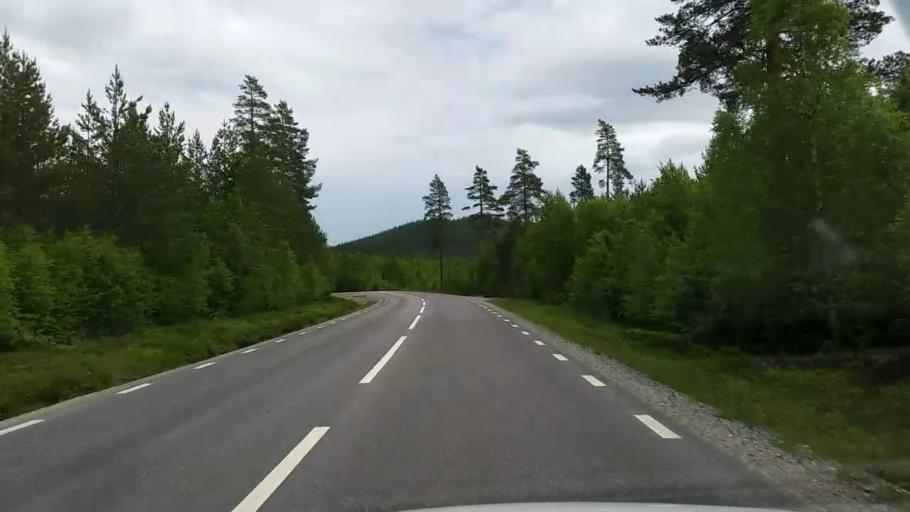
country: SE
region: Gaevleborg
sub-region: Bollnas Kommun
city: Vittsjo
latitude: 60.9423
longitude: 16.3669
